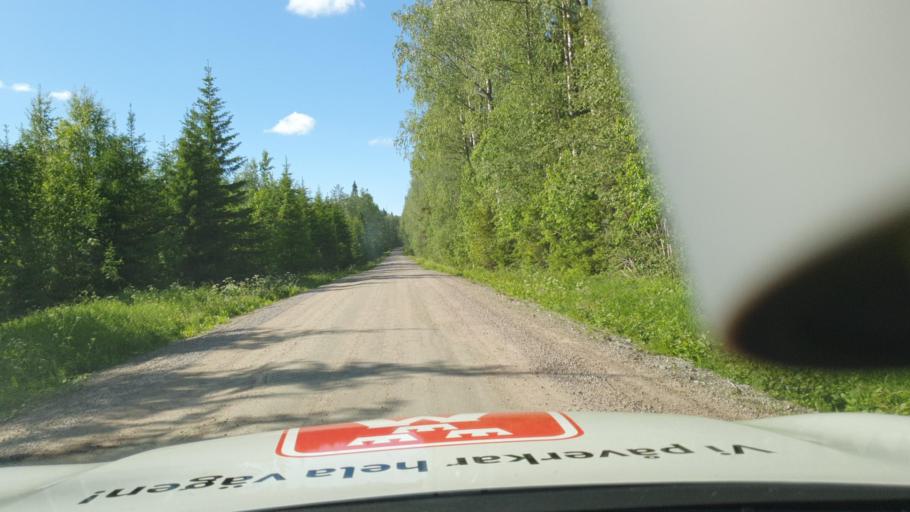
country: SE
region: Vaesterbotten
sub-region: Vannas Kommun
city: Vaennaes
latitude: 63.7831
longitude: 19.6307
